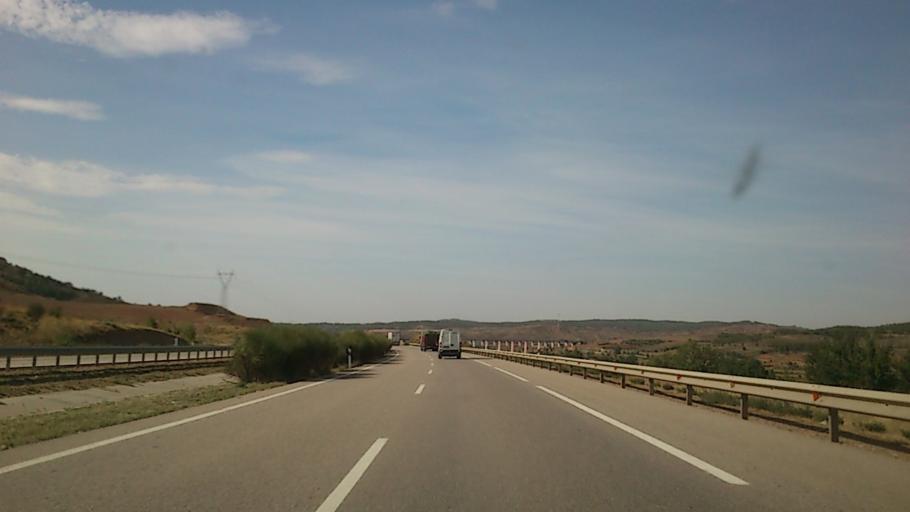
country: ES
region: Aragon
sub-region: Provincia de Teruel
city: Calamocha
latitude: 40.9329
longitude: -1.2677
